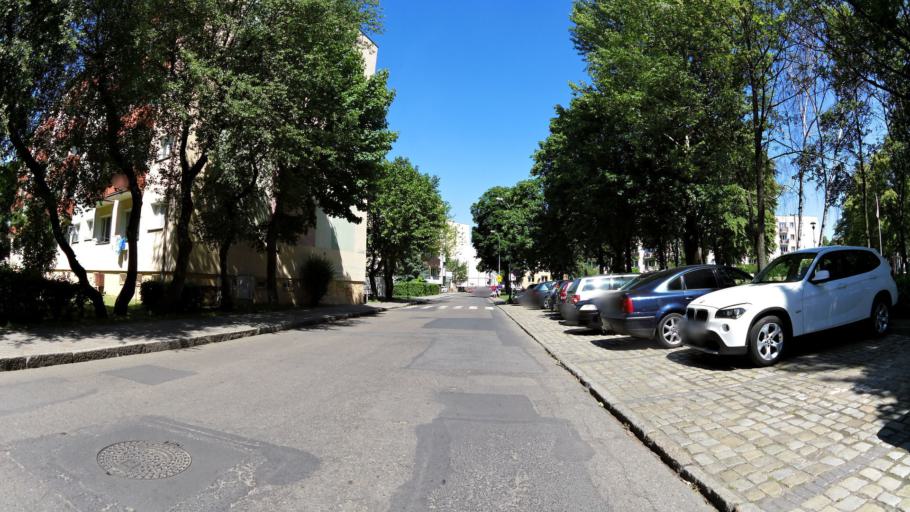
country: PL
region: Lubusz
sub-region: Powiat slubicki
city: Slubice
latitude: 52.3499
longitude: 14.5625
